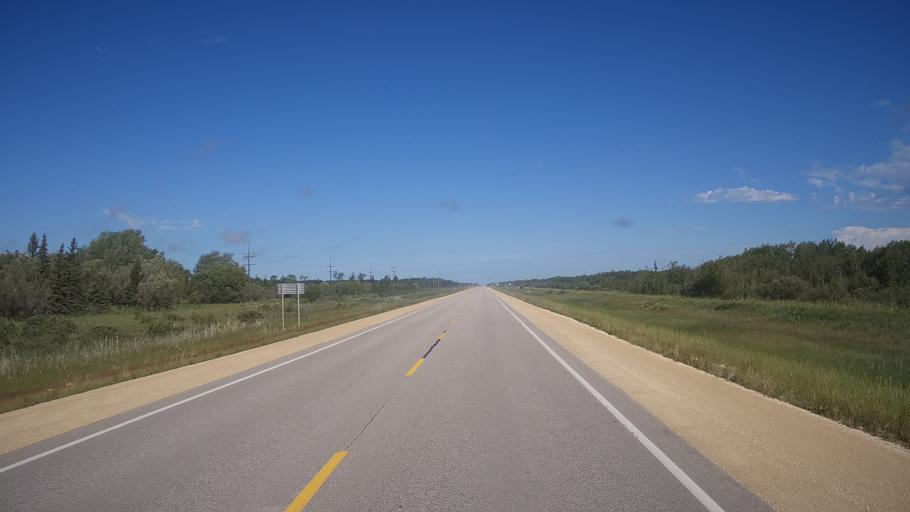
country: CA
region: Manitoba
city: Stonewall
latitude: 50.2360
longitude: -97.7068
